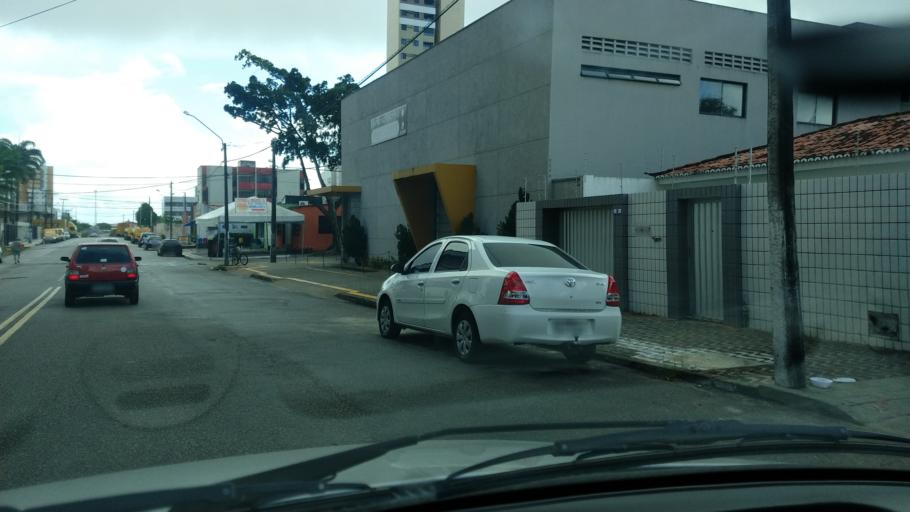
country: BR
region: Rio Grande do Norte
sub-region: Natal
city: Natal
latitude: -5.8132
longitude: -35.2194
